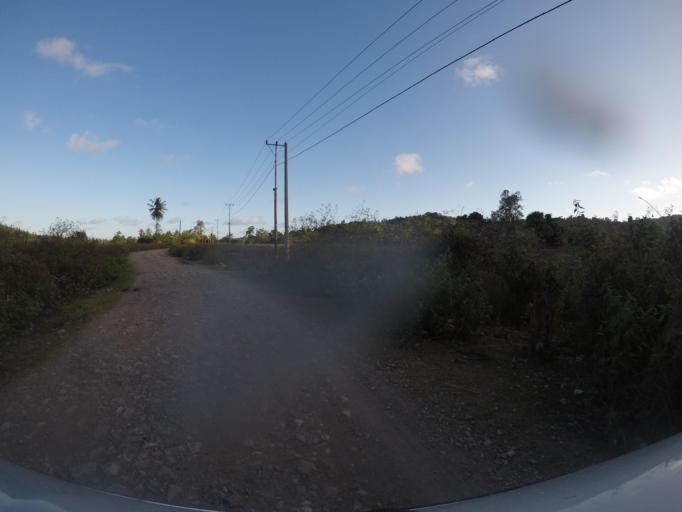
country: TL
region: Baucau
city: Venilale
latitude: -8.7281
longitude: 126.7084
